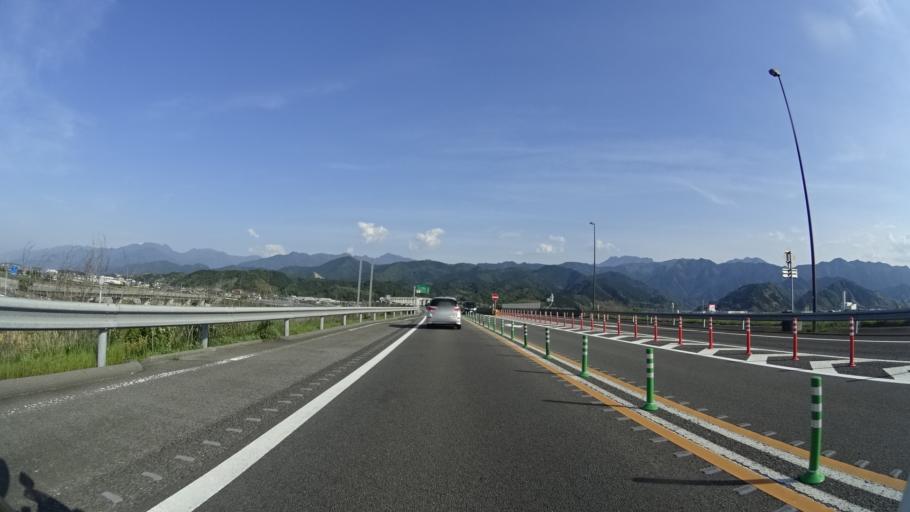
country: JP
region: Ehime
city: Saijo
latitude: 33.8974
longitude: 133.0782
